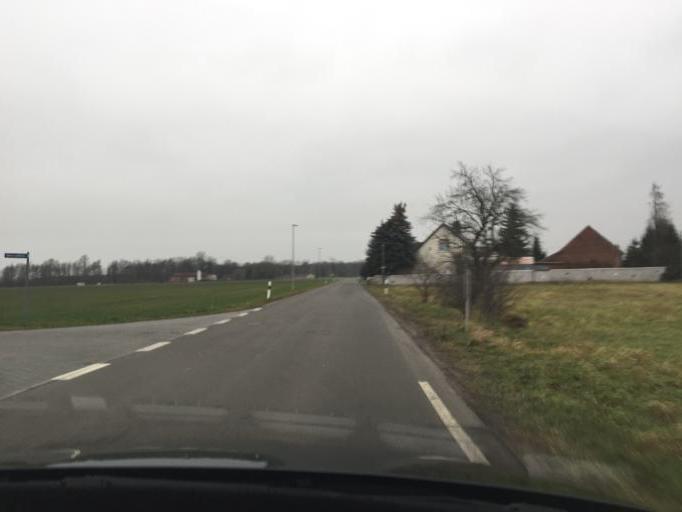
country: DE
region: Brandenburg
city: Vetschau
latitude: 51.7937
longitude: 14.0791
